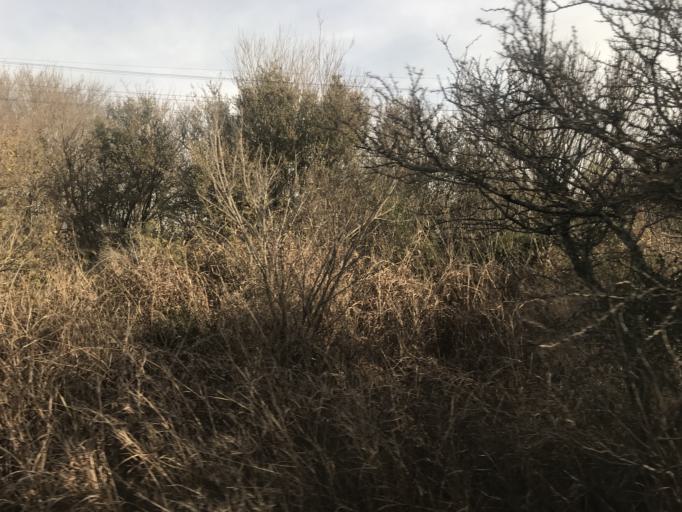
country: AR
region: Cordoba
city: Laguna Larga
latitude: -31.7565
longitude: -63.8209
